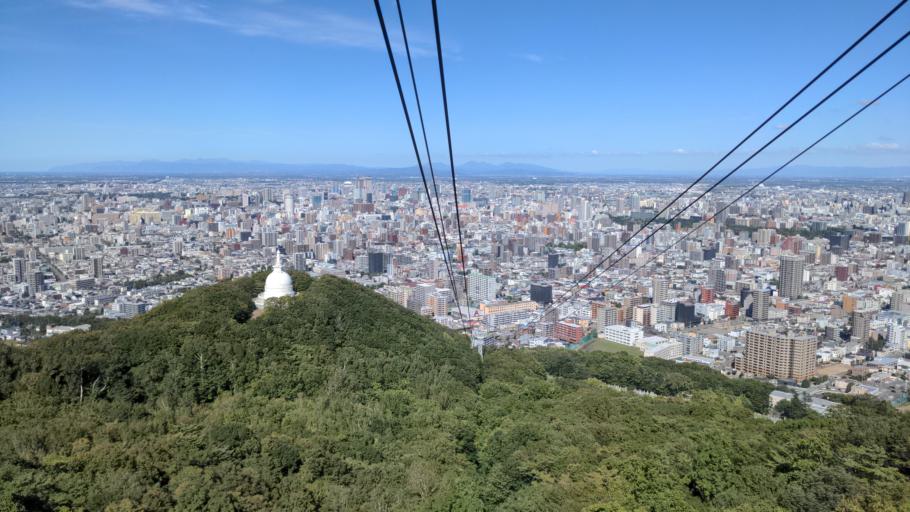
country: JP
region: Hokkaido
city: Sapporo
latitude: 43.0270
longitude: 141.3294
